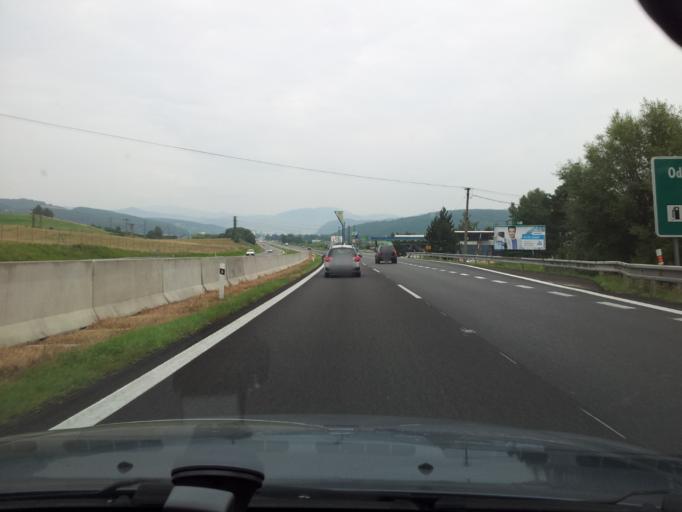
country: SK
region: Banskobystricky
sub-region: Okres Banska Bystrica
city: Banska Bystrica
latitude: 48.6652
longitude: 19.1328
